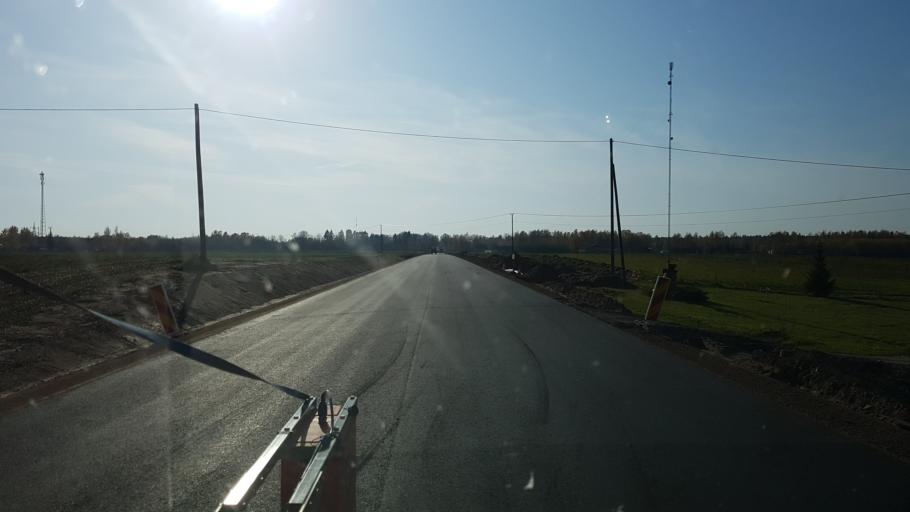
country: EE
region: Vorumaa
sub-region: Antsla vald
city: Vana-Antsla
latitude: 57.8394
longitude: 26.5484
